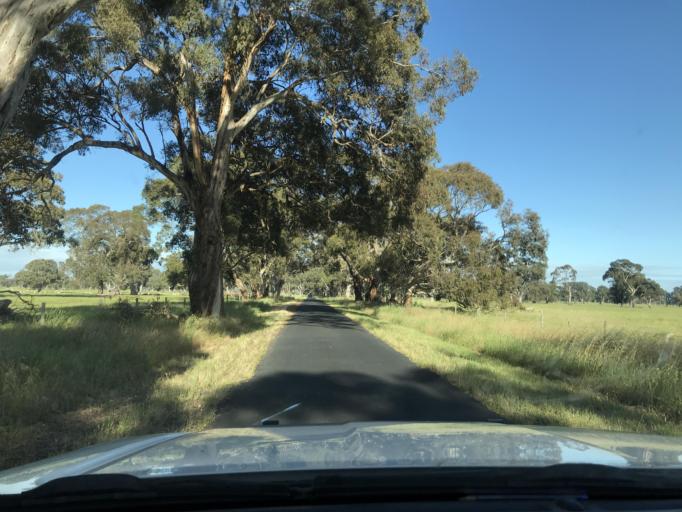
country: AU
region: South Australia
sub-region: Wattle Range
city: Penola
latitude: -37.2021
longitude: 140.9964
